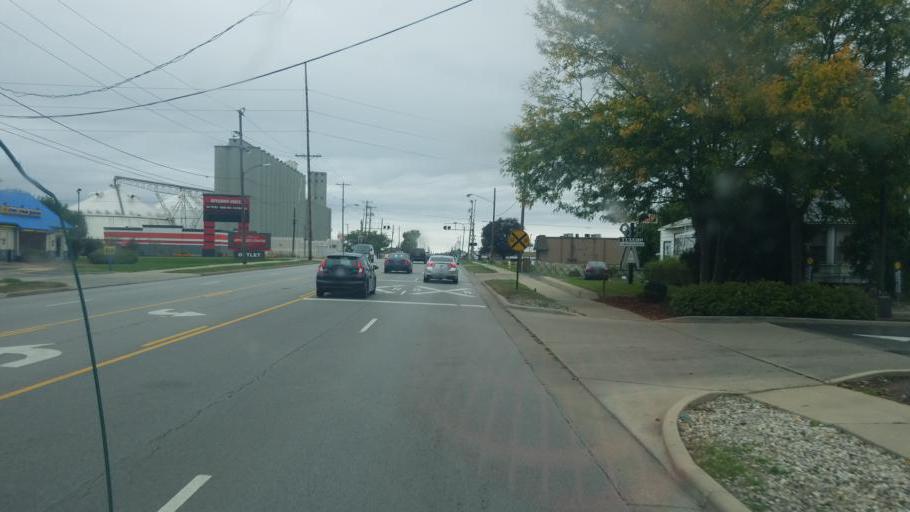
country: US
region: Ohio
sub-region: Lucas County
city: Maumee
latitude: 41.5685
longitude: -83.6569
